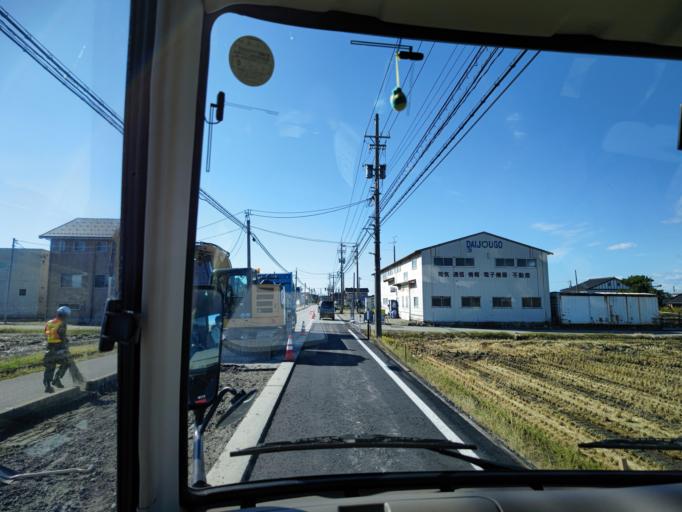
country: JP
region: Toyama
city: Nyuzen
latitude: 36.9005
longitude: 137.4219
